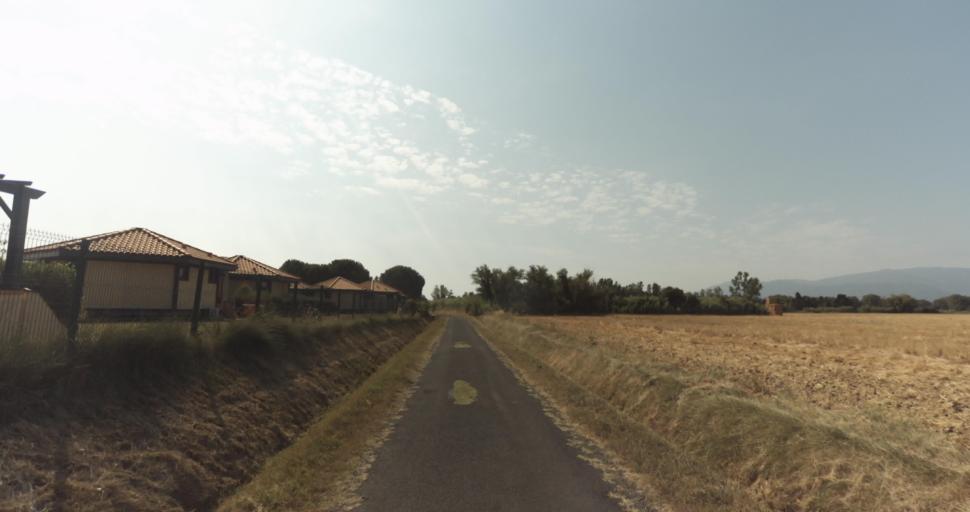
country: FR
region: Languedoc-Roussillon
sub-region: Departement des Pyrenees-Orientales
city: Latour-Bas-Elne
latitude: 42.6147
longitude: 3.0189
